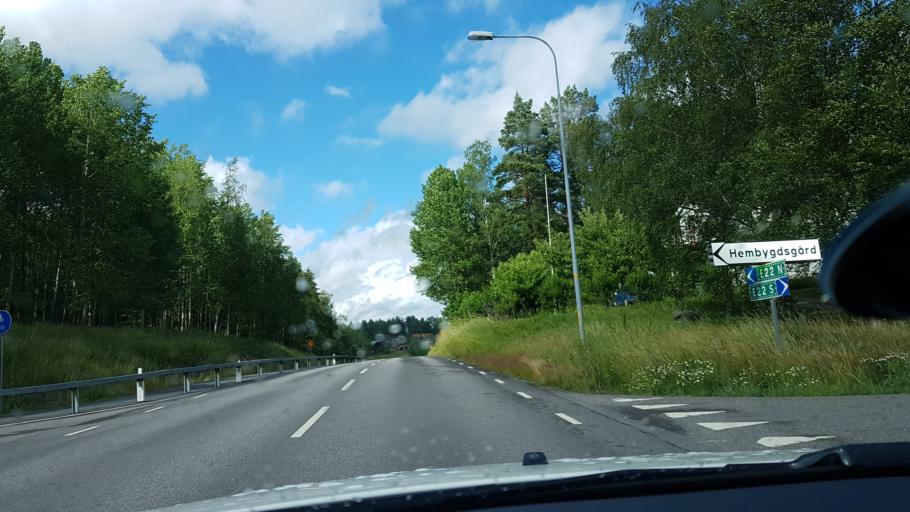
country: SE
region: OEstergoetland
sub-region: Valdemarsviks Kommun
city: Gusum
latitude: 58.2748
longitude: 16.5047
